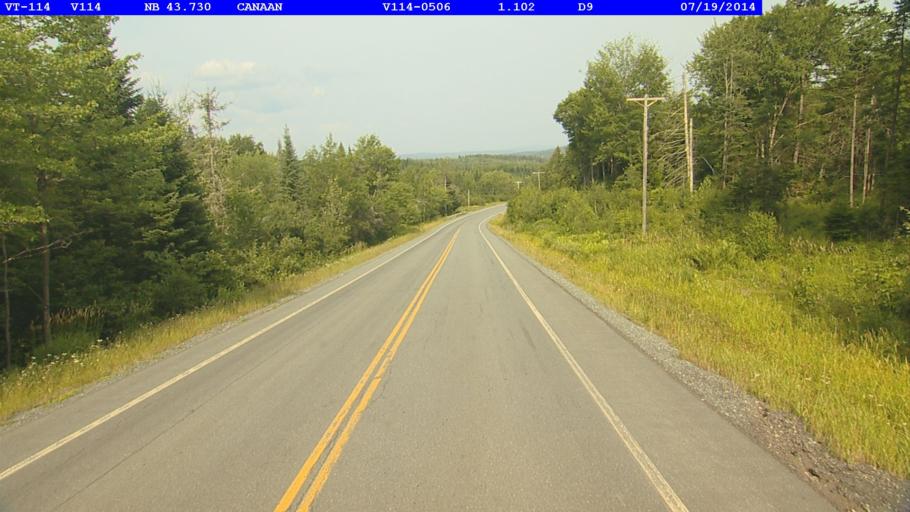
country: CA
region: Quebec
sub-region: Estrie
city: Coaticook
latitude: 45.0060
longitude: -71.6714
